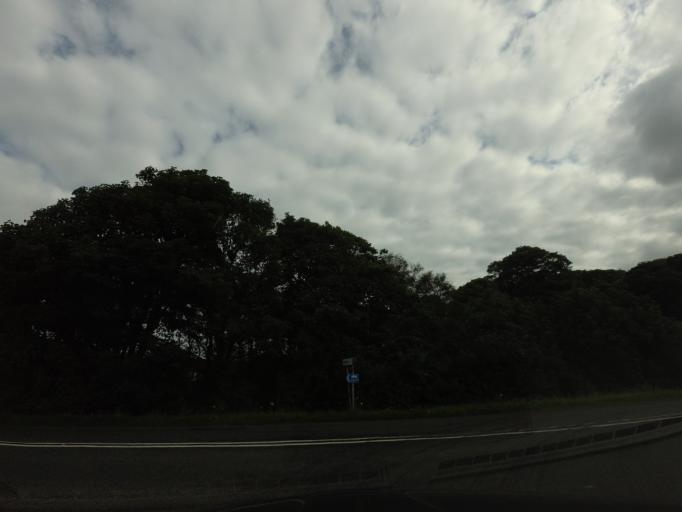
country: GB
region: Scotland
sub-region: Dumfries and Galloway
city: Annan
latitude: 54.9851
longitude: -3.2923
